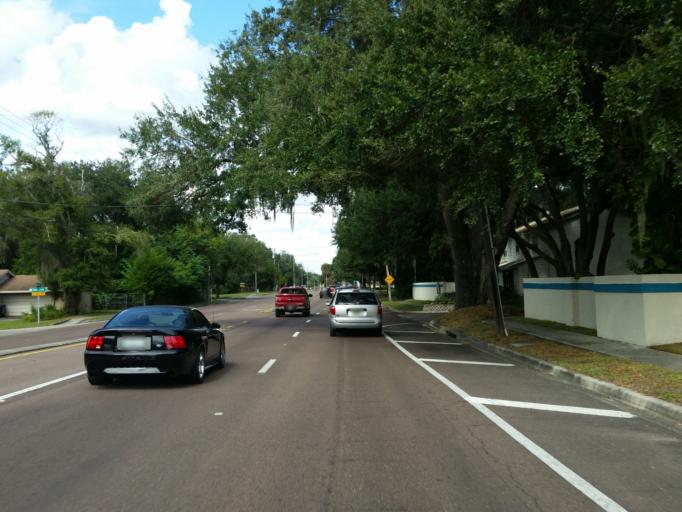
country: US
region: Florida
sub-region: Hillsborough County
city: Brandon
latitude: 27.9288
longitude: -82.2939
